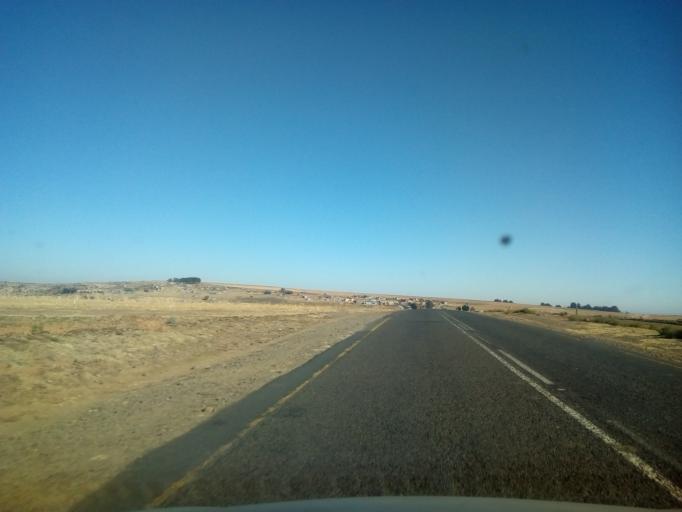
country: LS
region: Maseru
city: Maseru
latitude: -29.2930
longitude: 27.6278
